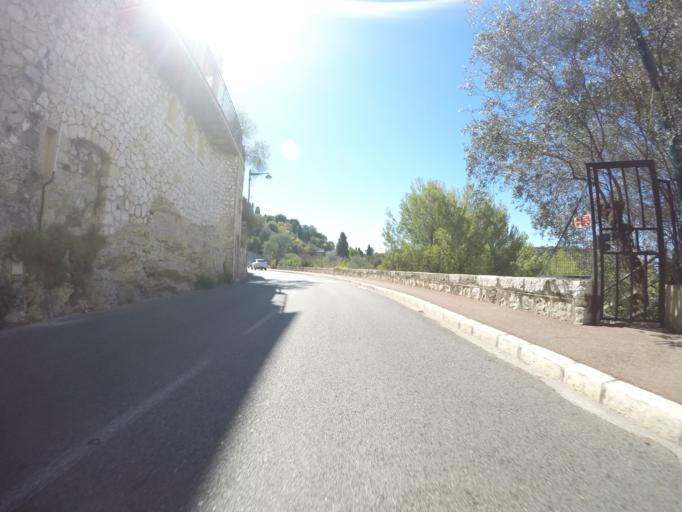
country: FR
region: Provence-Alpes-Cote d'Azur
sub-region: Departement des Alpes-Maritimes
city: Saint-Jean-Cap-Ferrat
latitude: 43.6976
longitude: 7.3265
